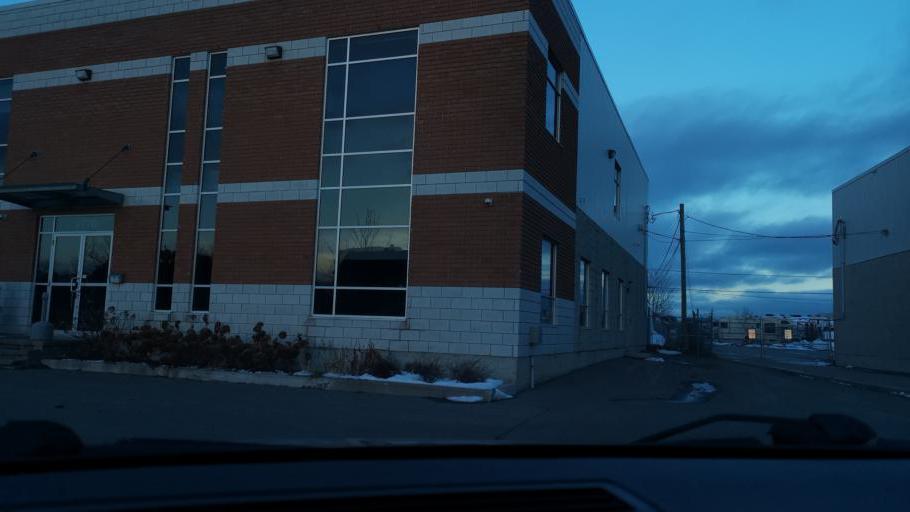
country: CA
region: Quebec
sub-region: Laurentides
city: Rosemere
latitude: 45.5788
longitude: -73.7594
